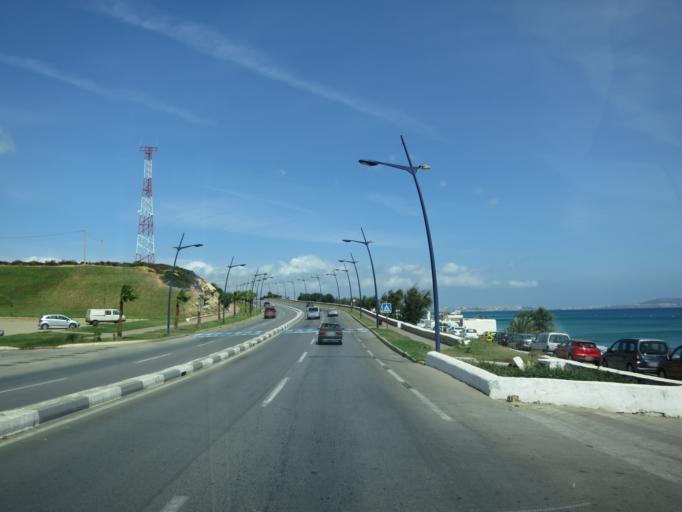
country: ES
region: Ceuta
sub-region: Ceuta
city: Ceuta
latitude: 35.7794
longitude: -5.3485
